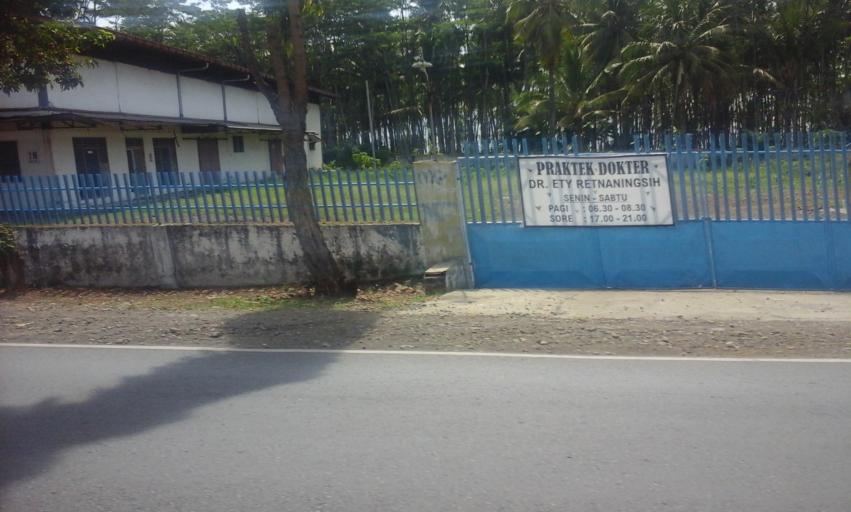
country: ID
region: East Java
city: Klatakan
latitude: -8.1553
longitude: 114.3952
